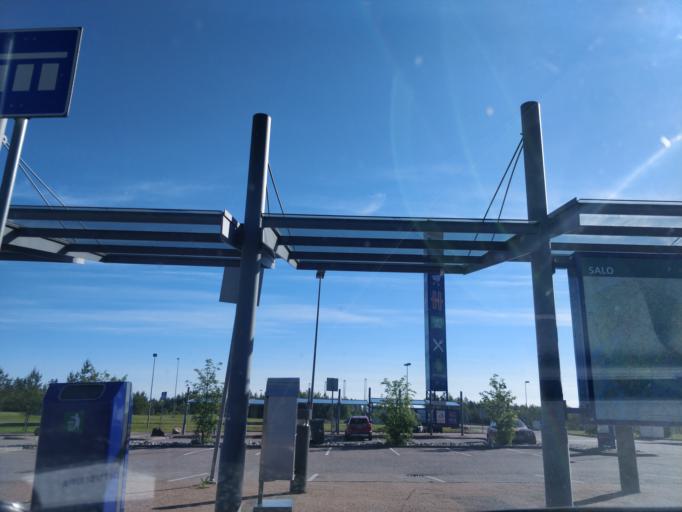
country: FI
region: Varsinais-Suomi
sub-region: Salo
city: Suomusjaervi
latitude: 60.3806
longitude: 23.6148
